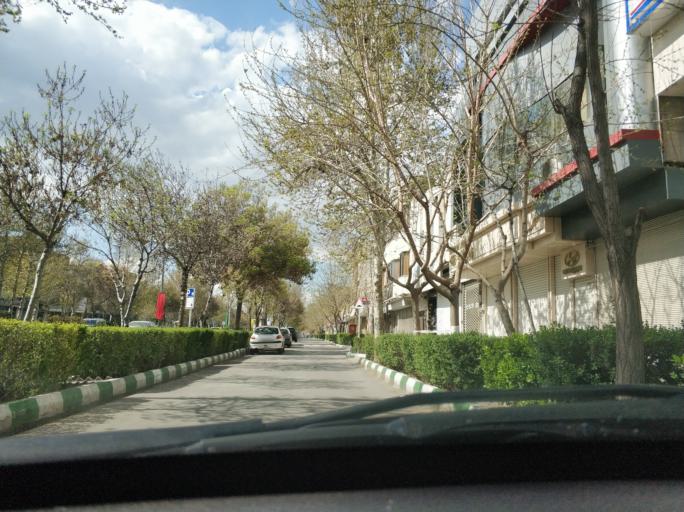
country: IR
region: Razavi Khorasan
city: Mashhad
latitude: 36.2714
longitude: 59.5955
